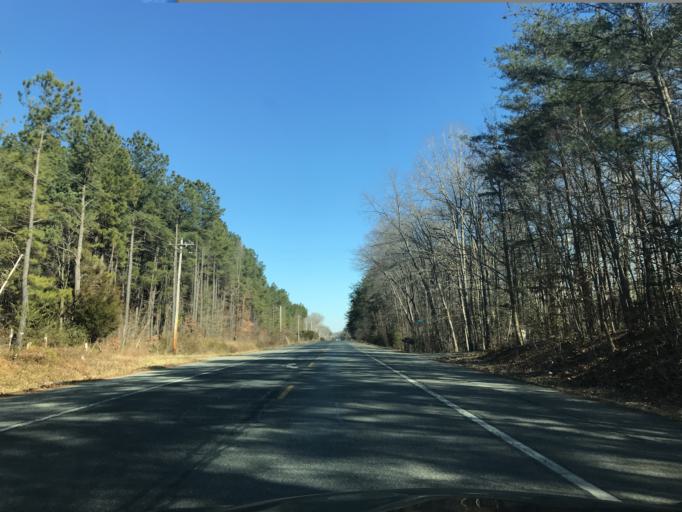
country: US
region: Virginia
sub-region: Prince William County
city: Cherry Hill
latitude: 38.5338
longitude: -77.2041
